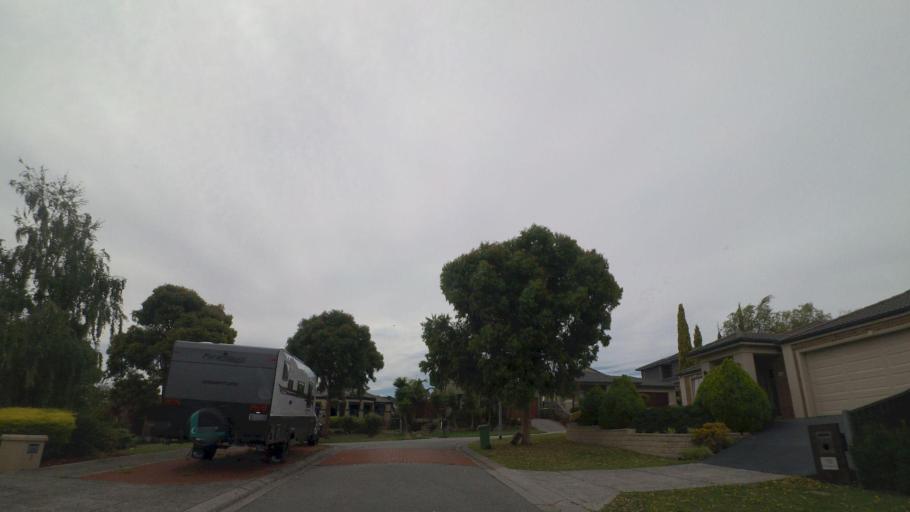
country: AU
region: Victoria
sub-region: Yarra Ranges
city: Kilsyth
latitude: -37.7819
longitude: 145.3413
